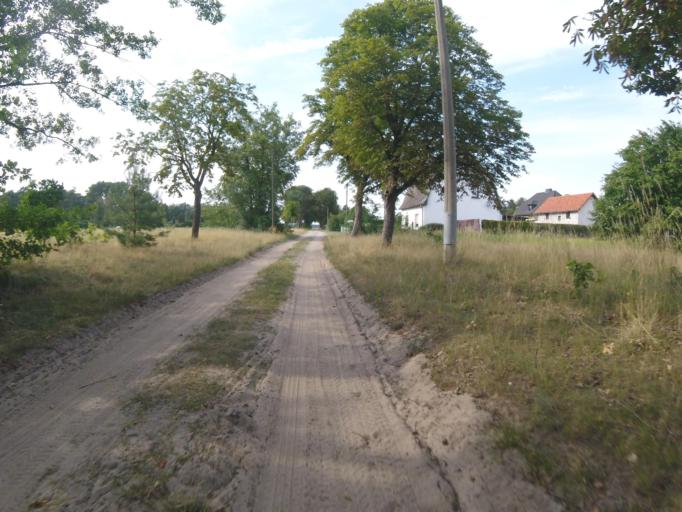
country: DE
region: Brandenburg
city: Spreenhagen
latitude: 52.2730
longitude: 13.8198
